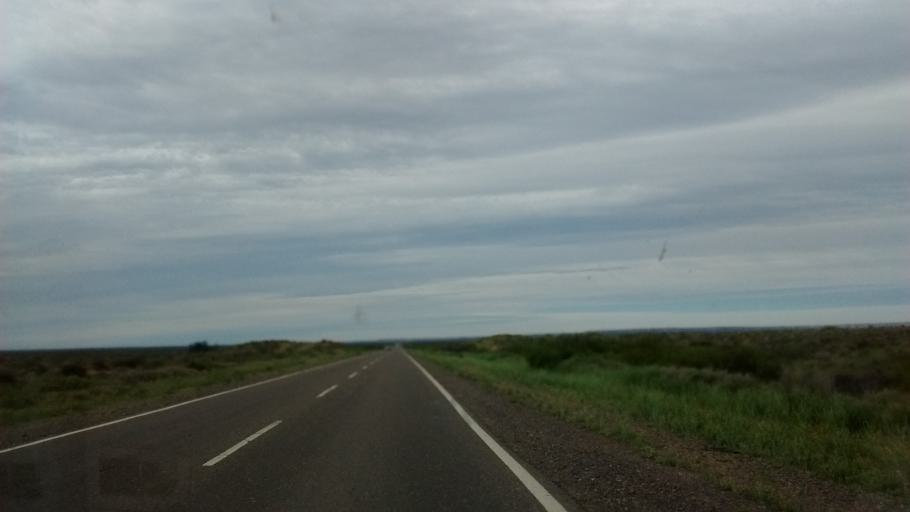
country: AR
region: Rio Negro
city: Catriel
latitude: -38.0377
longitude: -67.9176
